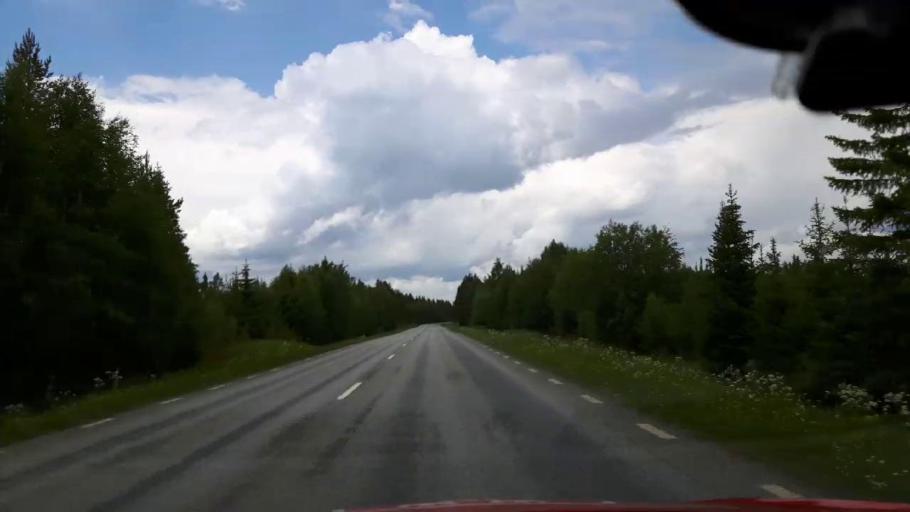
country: SE
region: Jaemtland
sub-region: Krokoms Kommun
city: Krokom
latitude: 63.3569
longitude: 14.4131
